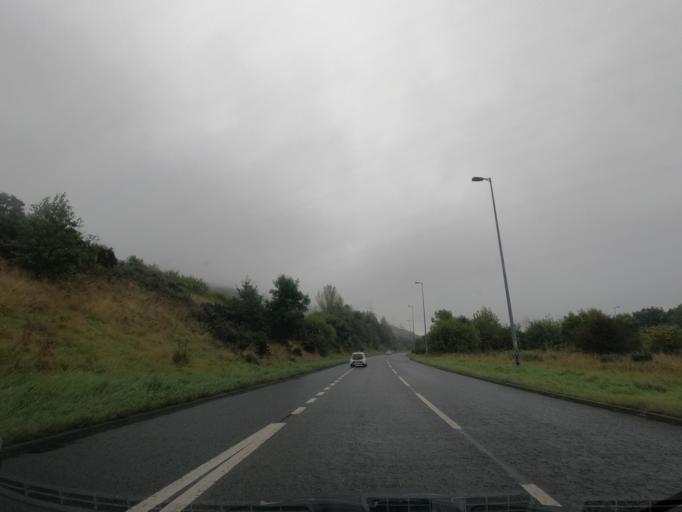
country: GB
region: England
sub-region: Redcar and Cleveland
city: South Bank
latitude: 54.5652
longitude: -1.1223
